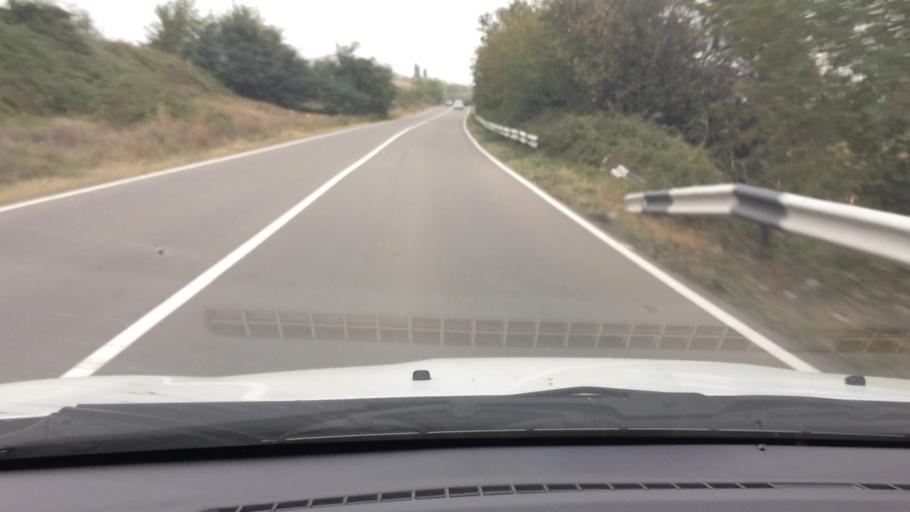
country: AM
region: Tavush
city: Bagratashen
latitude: 41.2699
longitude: 44.7909
